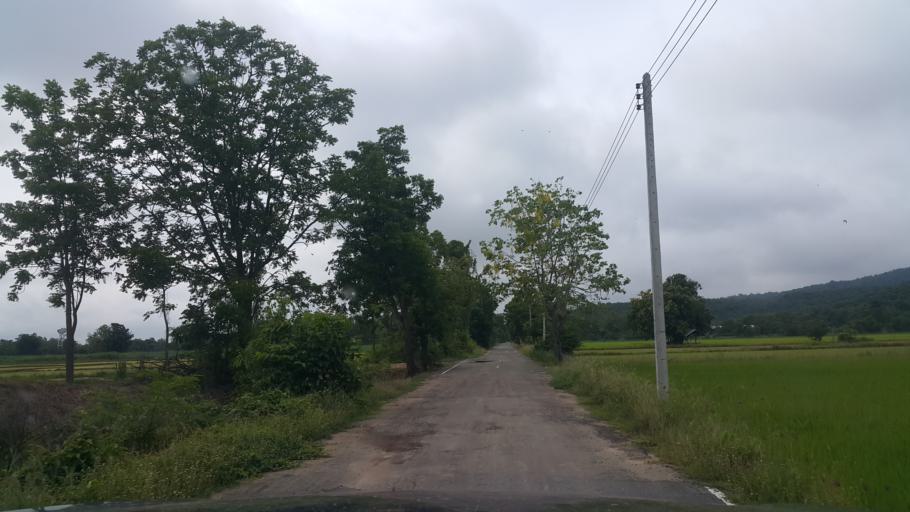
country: TH
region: Sukhothai
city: Sawankhalok
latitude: 17.3086
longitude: 99.7028
